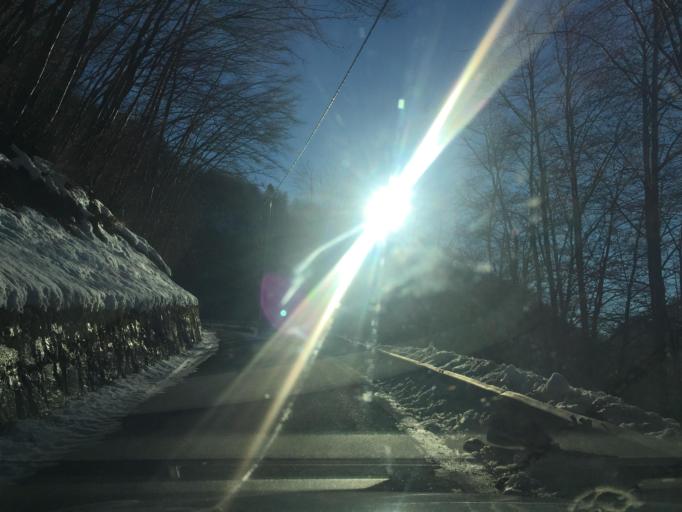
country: IT
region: Friuli Venezia Giulia
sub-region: Provincia di Udine
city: Lauco
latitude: 46.4370
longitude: 12.9714
